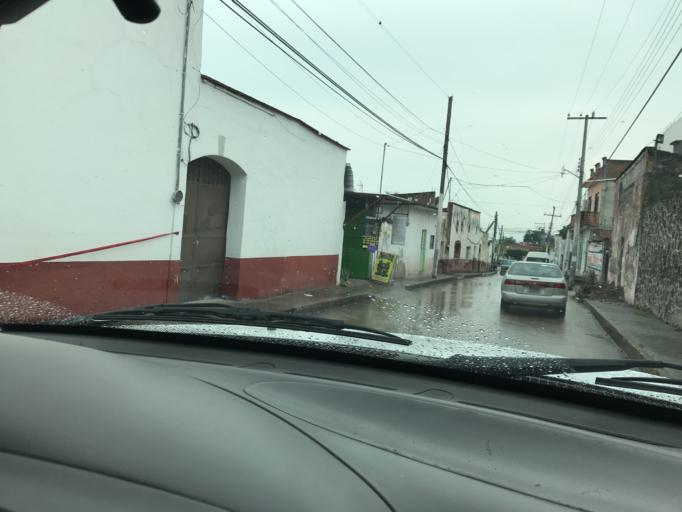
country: MX
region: Morelos
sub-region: Ayala
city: Ciudad Ayala
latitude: 18.7661
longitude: -98.9844
